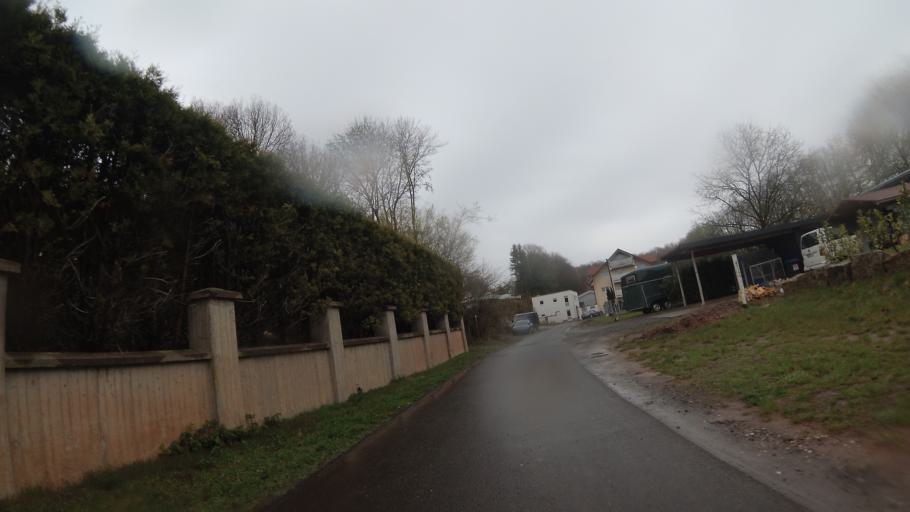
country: DE
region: Saarland
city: Tholey
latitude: 49.4875
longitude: 7.0468
